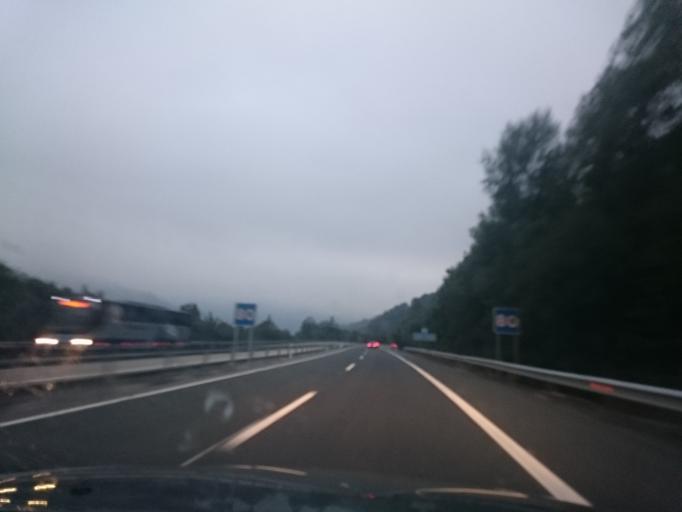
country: ES
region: Asturias
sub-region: Province of Asturias
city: Pola de Lena
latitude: 43.0417
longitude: -5.8193
